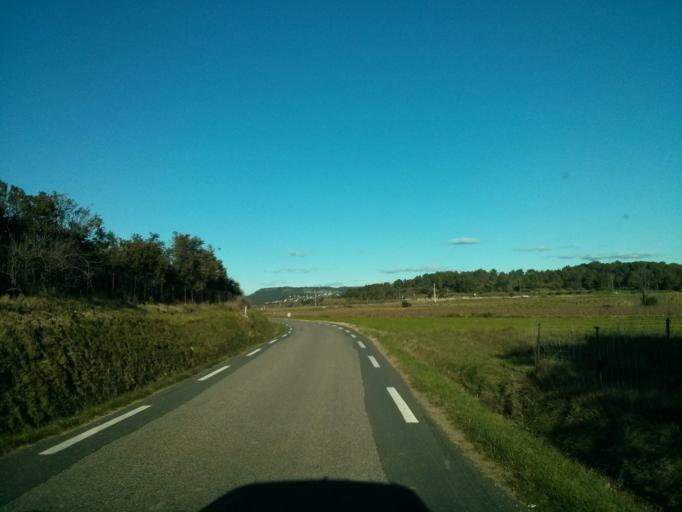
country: FR
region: Languedoc-Roussillon
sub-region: Departement du Gard
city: Mus
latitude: 43.7573
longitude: 4.1997
